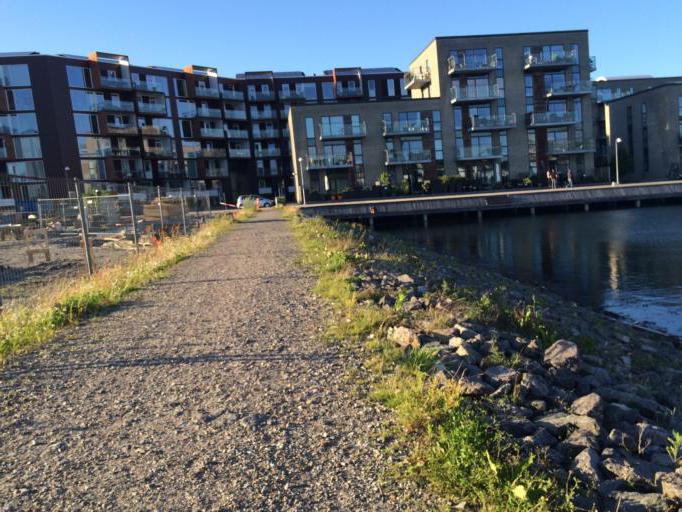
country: DK
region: South Denmark
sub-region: Vejle Kommune
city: Vejle
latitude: 55.7074
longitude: 9.5533
